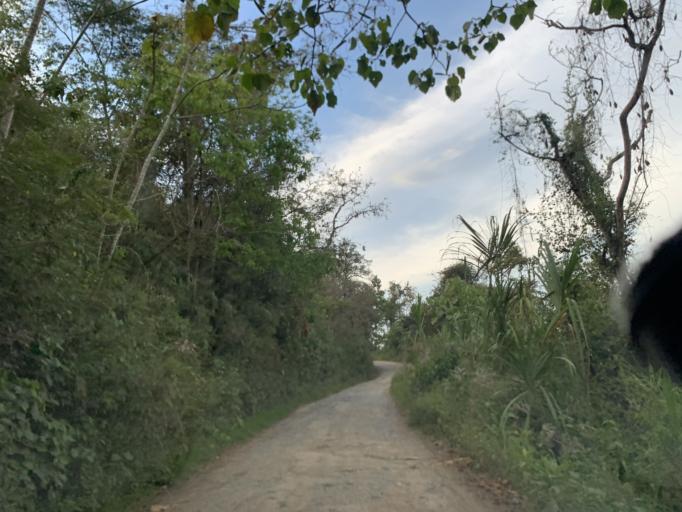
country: CO
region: Boyaca
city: Santana
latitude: 6.0766
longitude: -73.4870
